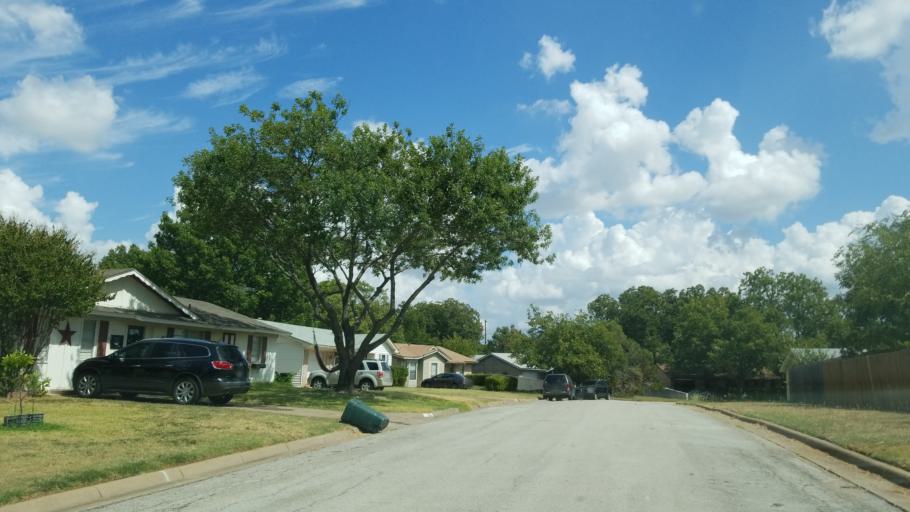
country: US
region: Texas
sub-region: Tarrant County
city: Euless
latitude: 32.8554
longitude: -97.0931
